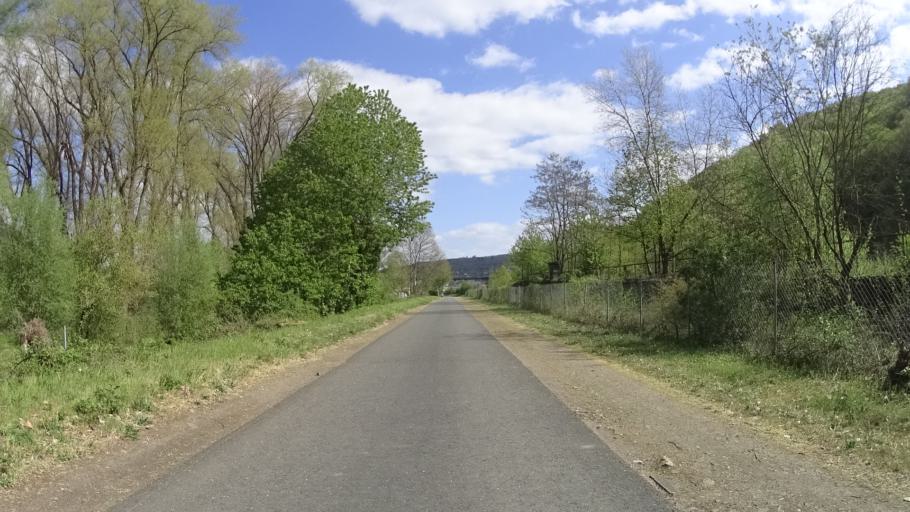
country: DE
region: Rheinland-Pfalz
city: Weiler
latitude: 49.9717
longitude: 7.8746
